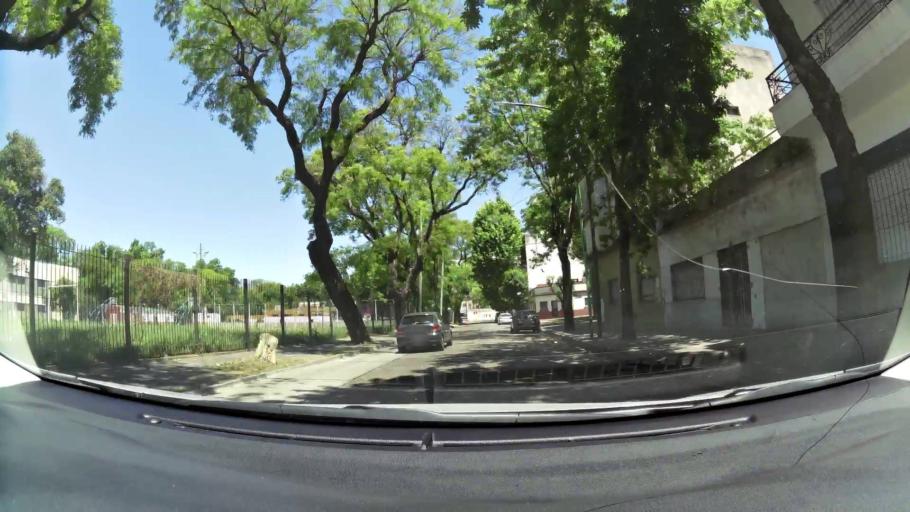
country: AR
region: Buenos Aires
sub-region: Partido de Avellaneda
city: Avellaneda
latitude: -34.6487
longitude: -58.3901
